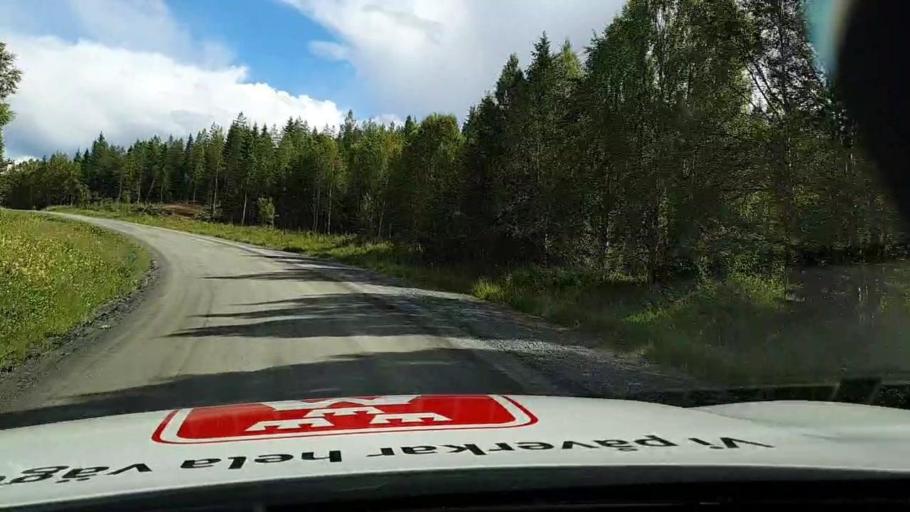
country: SE
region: Jaemtland
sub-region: Krokoms Kommun
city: Valla
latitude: 63.6780
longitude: 13.6816
